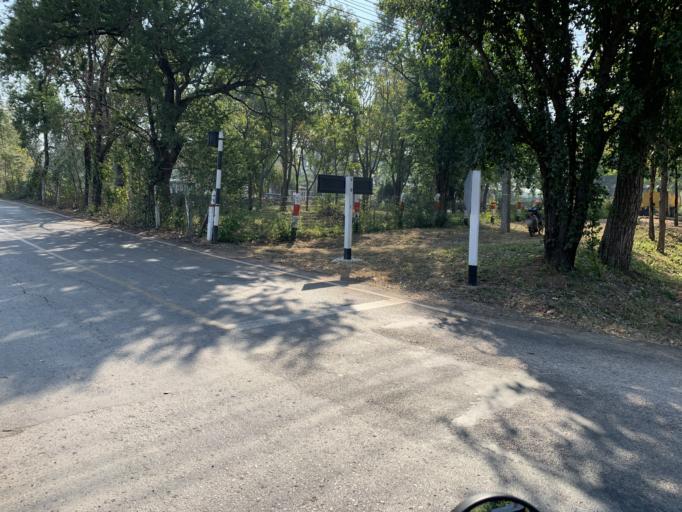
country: TH
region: Phetchabun
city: Phetchabun
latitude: 16.5296
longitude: 101.1577
